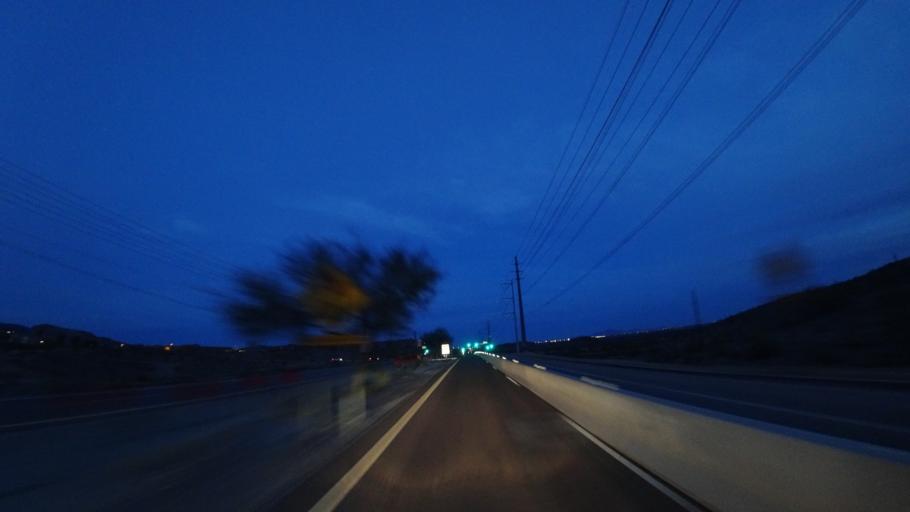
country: US
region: Arizona
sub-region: Maricopa County
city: Laveen
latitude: 33.2910
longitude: -112.0656
